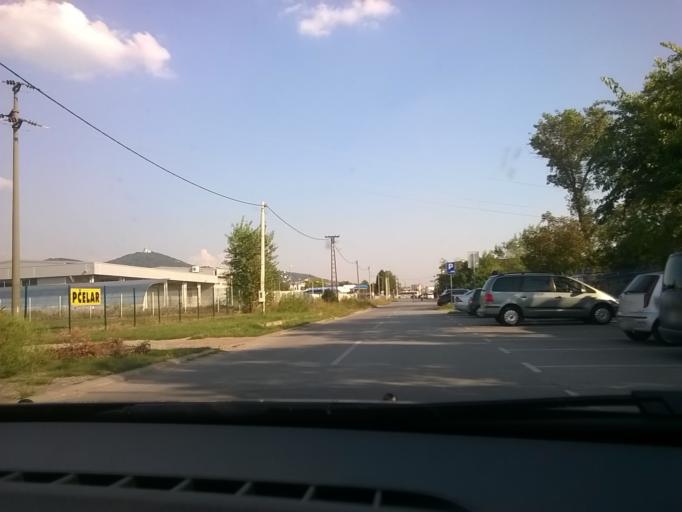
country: RS
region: Autonomna Pokrajina Vojvodina
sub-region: Juznobanatski Okrug
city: Vrsac
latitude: 45.1292
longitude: 21.2857
